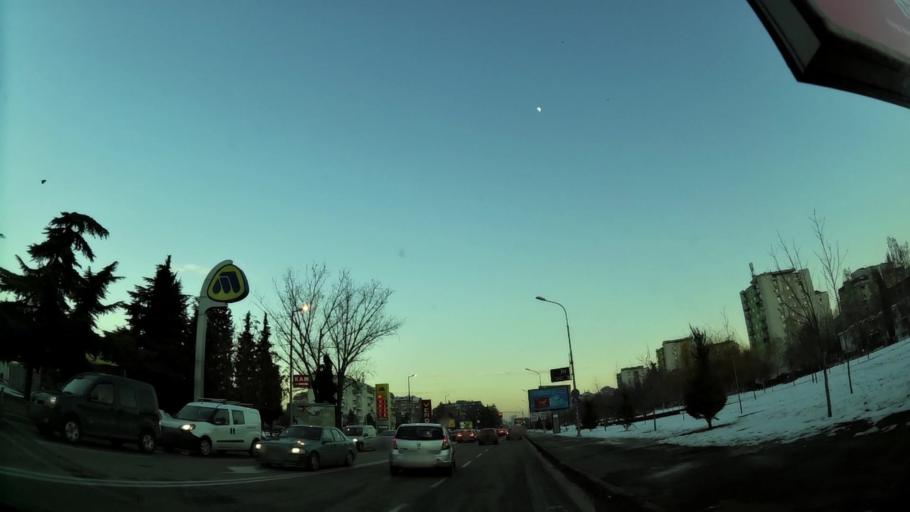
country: MK
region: Karpos
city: Skopje
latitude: 41.9964
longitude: 21.4040
